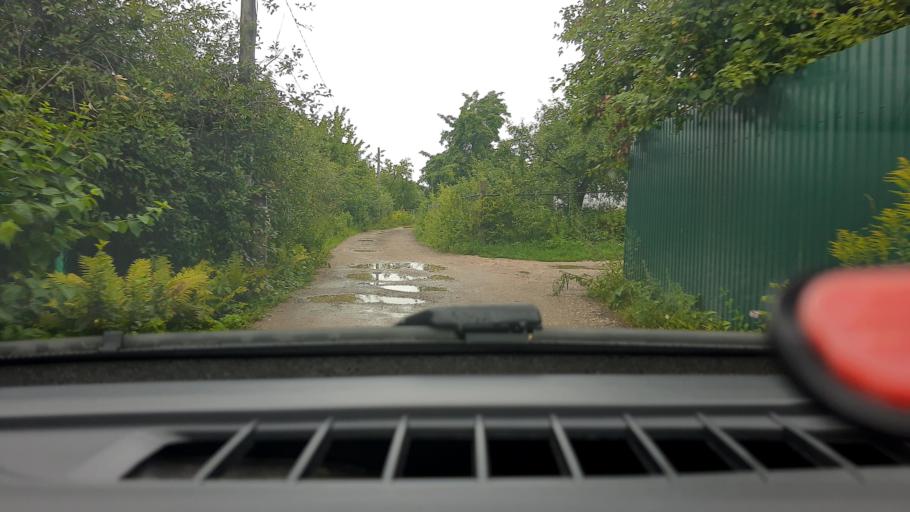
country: RU
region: Nizjnij Novgorod
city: Gorbatovka
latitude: 56.3152
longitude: 43.8363
